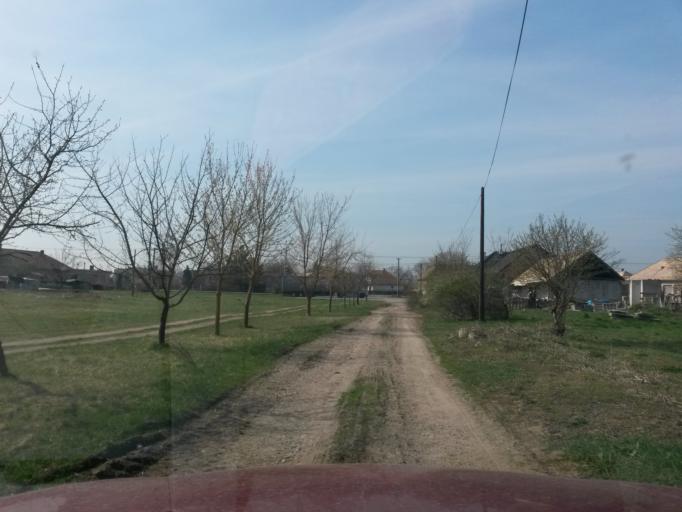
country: SK
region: Nitriansky
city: Levice
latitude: 48.1551
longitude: 18.5843
